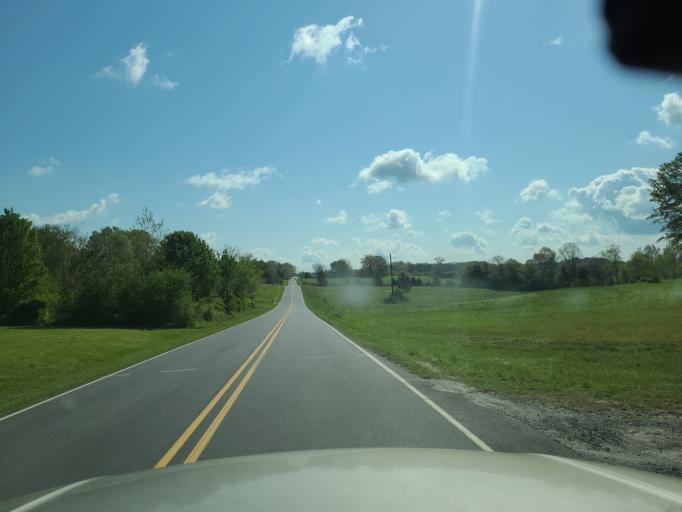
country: US
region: North Carolina
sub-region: Rutherford County
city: Spindale
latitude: 35.2965
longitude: -81.9265
